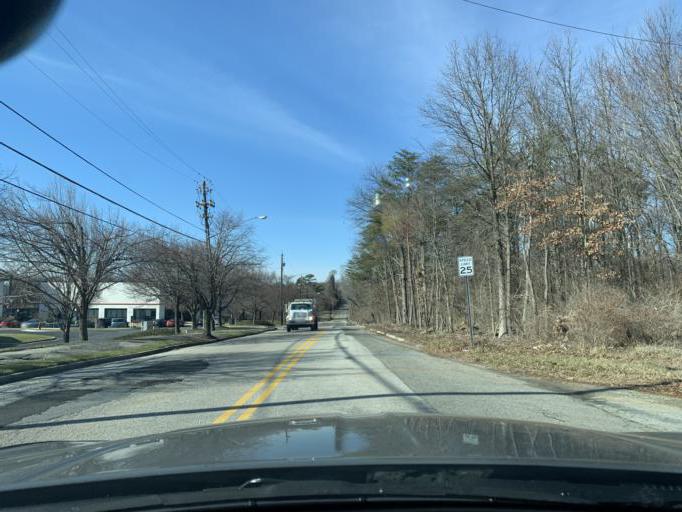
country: US
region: Maryland
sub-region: Prince George's County
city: Beltsville
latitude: 39.0643
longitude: -76.8912
